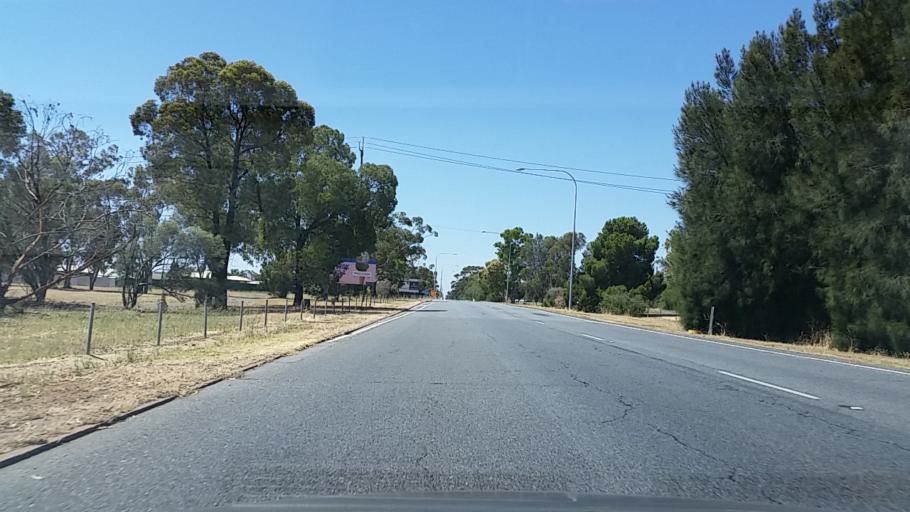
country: AU
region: South Australia
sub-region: Playford
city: Smithfield
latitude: -34.6959
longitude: 138.6854
